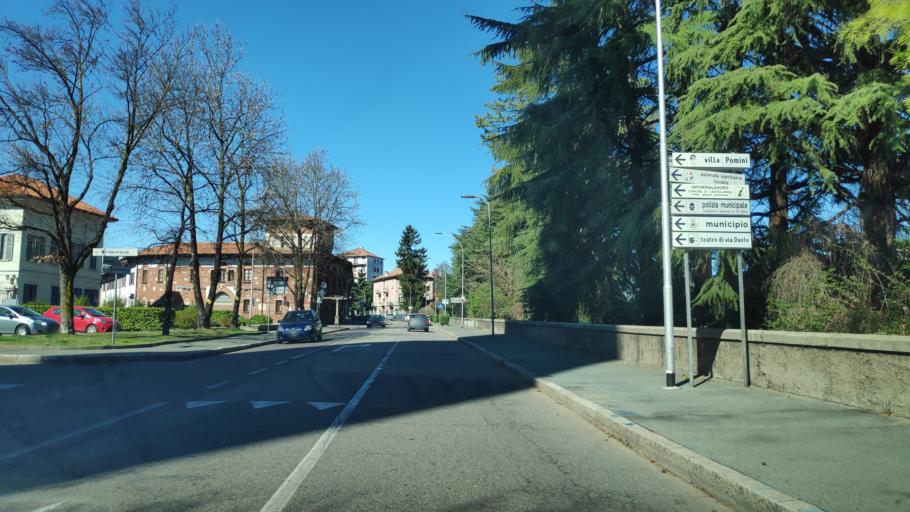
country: IT
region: Lombardy
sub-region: Provincia di Varese
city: Castellanza
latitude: 45.6124
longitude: 8.9002
